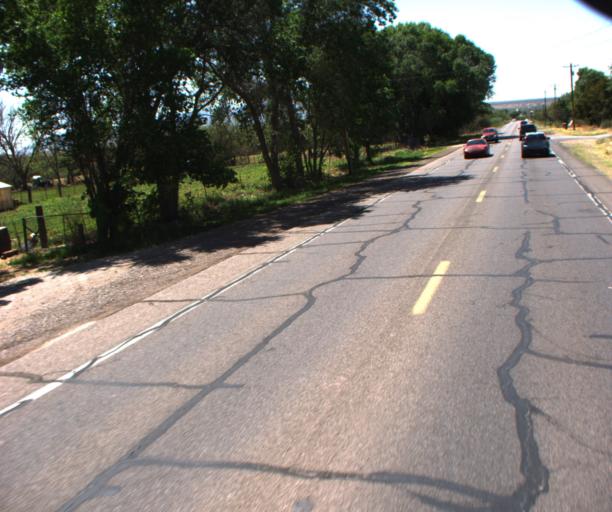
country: US
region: Arizona
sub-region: Cochise County
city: Saint David
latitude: 31.9054
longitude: -110.2415
